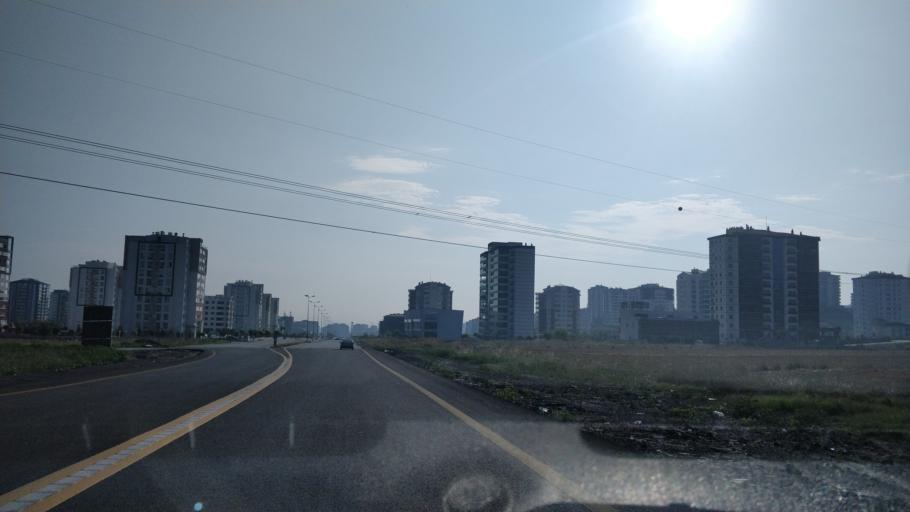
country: TR
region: Ankara
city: Etimesgut
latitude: 39.8861
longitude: 32.6135
